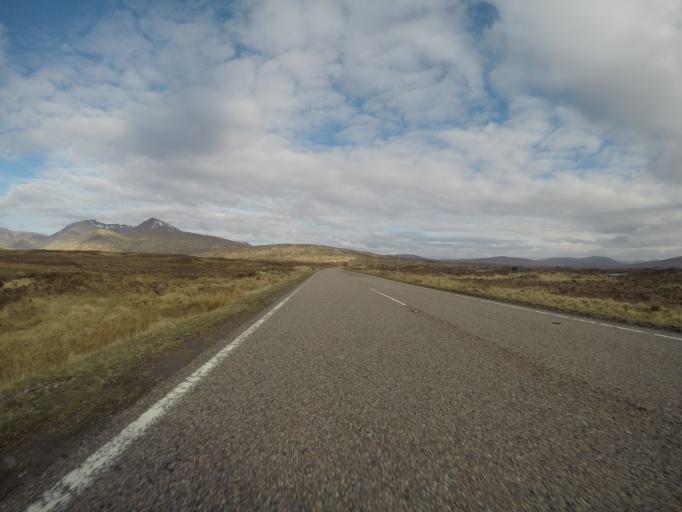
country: GB
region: Scotland
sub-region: Highland
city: Spean Bridge
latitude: 56.6010
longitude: -4.7492
